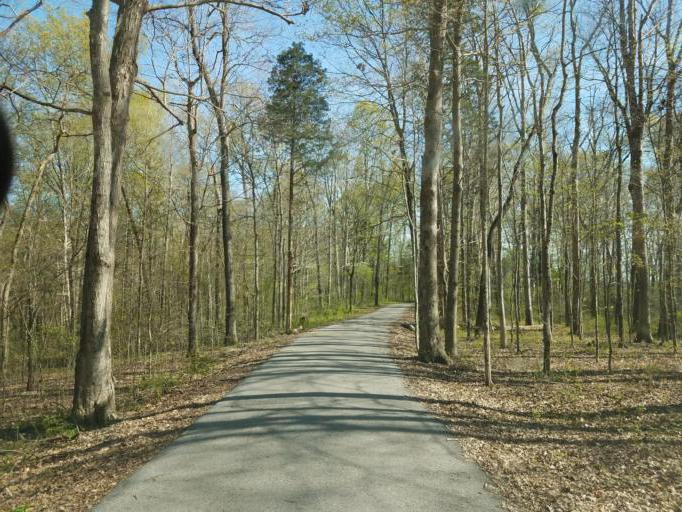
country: US
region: Kentucky
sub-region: Edmonson County
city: Brownsville
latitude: 37.1322
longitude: -86.1471
